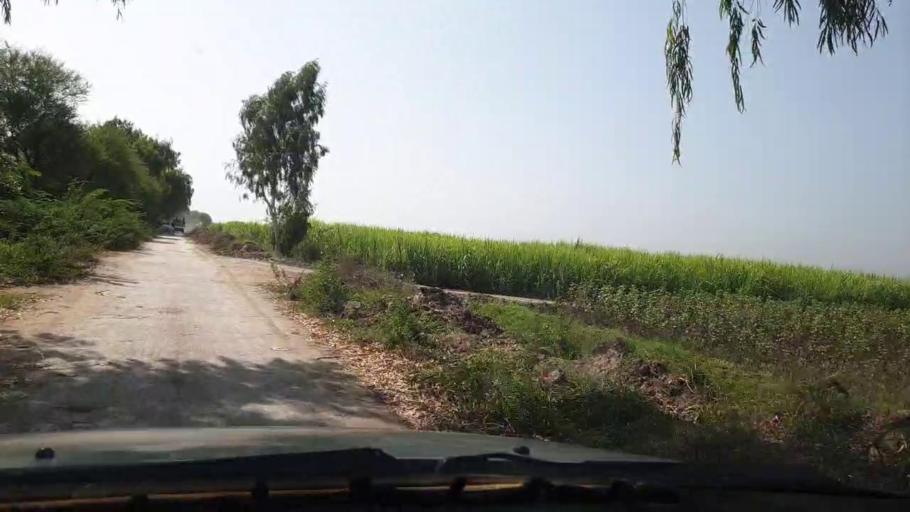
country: PK
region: Sindh
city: Chambar
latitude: 25.2446
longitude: 68.9155
